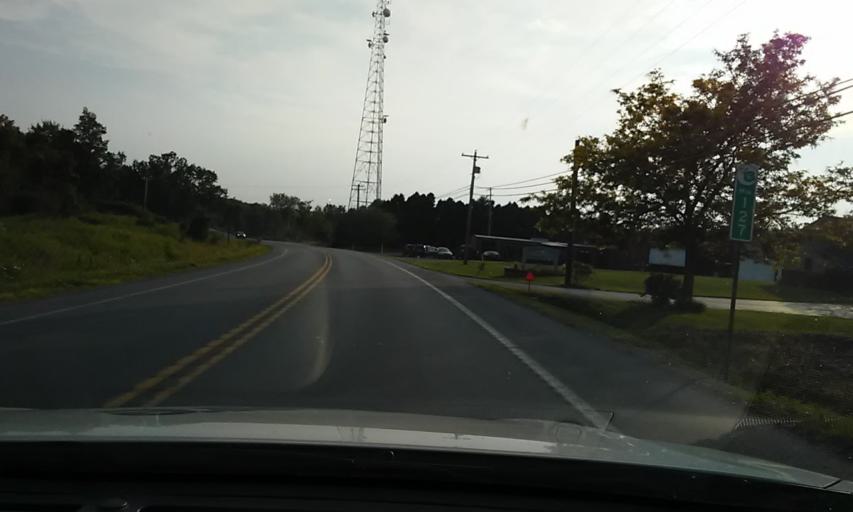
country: US
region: Pennsylvania
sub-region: McKean County
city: Kane
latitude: 41.6728
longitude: -78.7652
